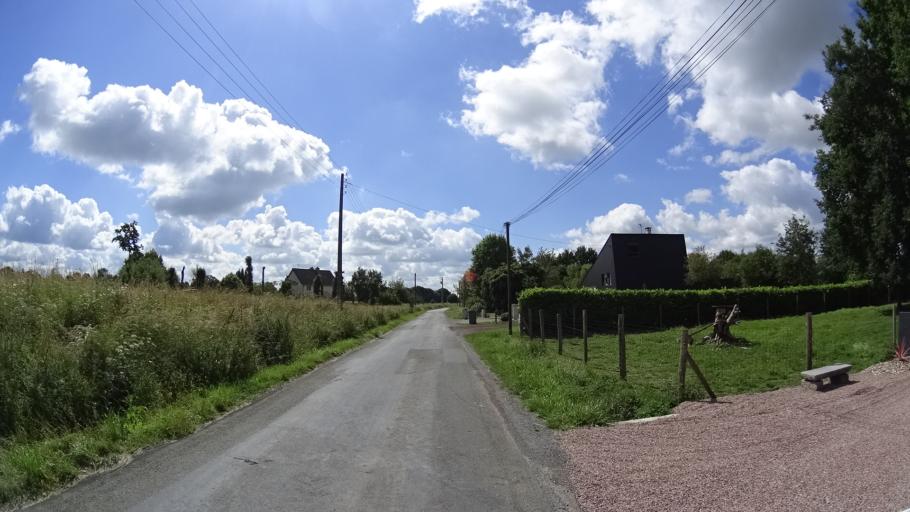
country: FR
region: Brittany
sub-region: Departement d'Ille-et-Vilaine
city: Le Rheu
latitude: 48.1159
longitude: -1.8164
